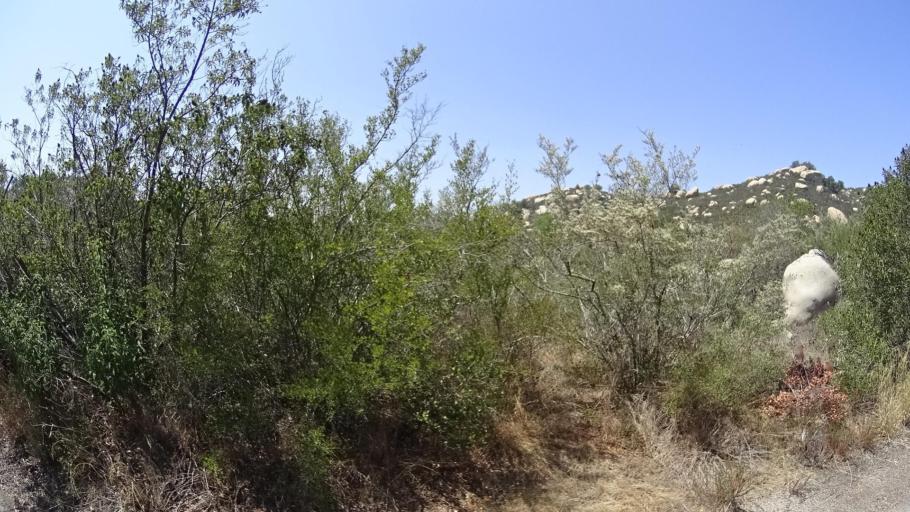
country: US
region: California
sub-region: San Diego County
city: Fallbrook
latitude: 33.4330
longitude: -117.2775
